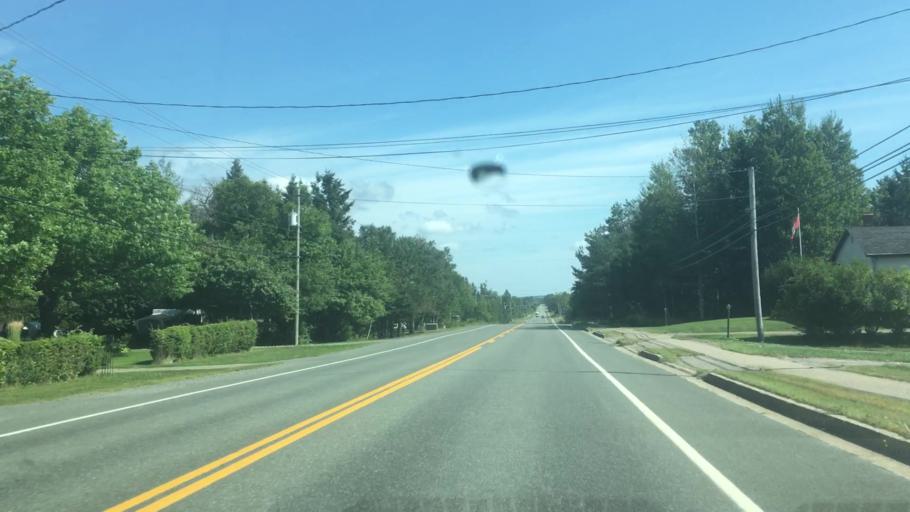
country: CA
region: Nova Scotia
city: Sydney
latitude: 46.0527
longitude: -60.3178
